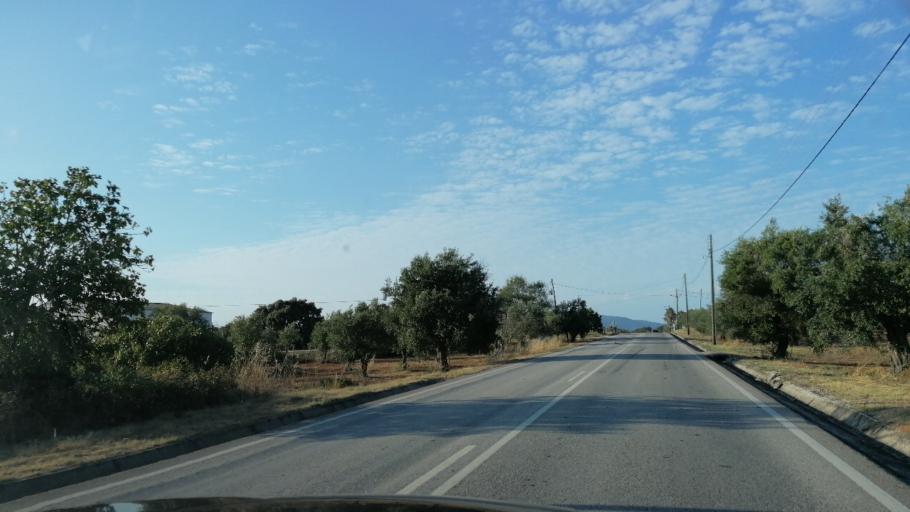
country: PT
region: Santarem
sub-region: Alcanena
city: Alcanena
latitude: 39.4172
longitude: -8.6366
